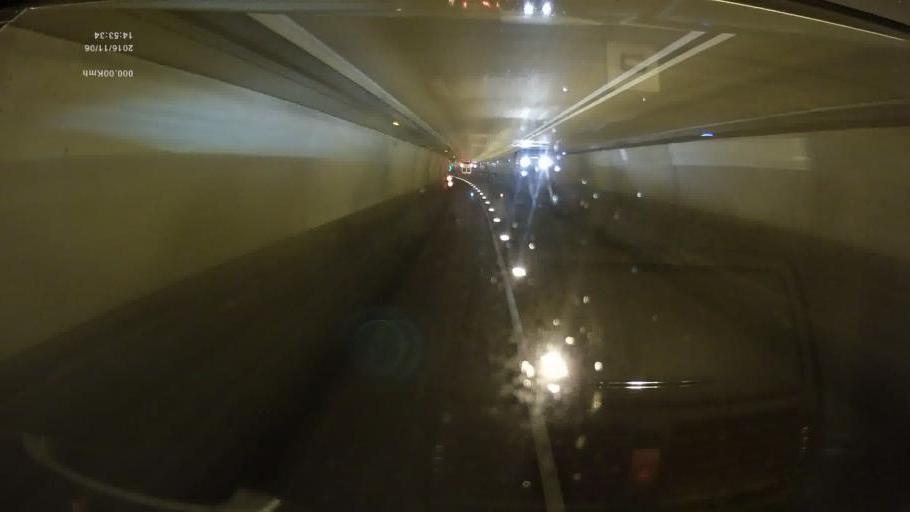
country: SK
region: Kosicky
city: Krompachy
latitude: 49.0068
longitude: 20.8619
